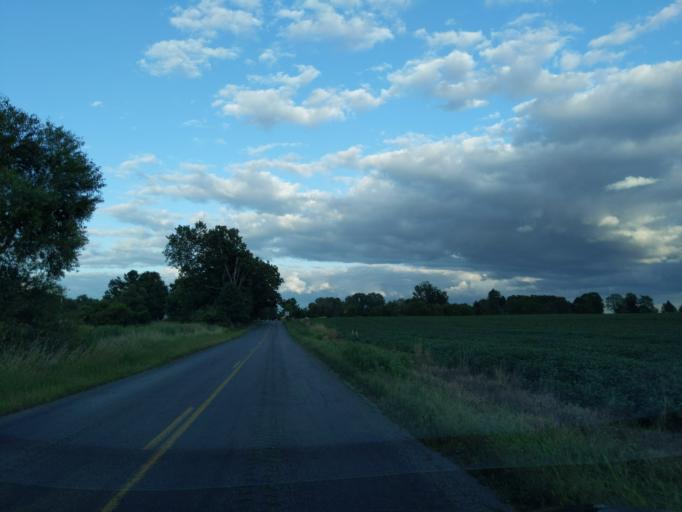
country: US
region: Michigan
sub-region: Ingham County
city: Holt
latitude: 42.5968
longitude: -84.5489
